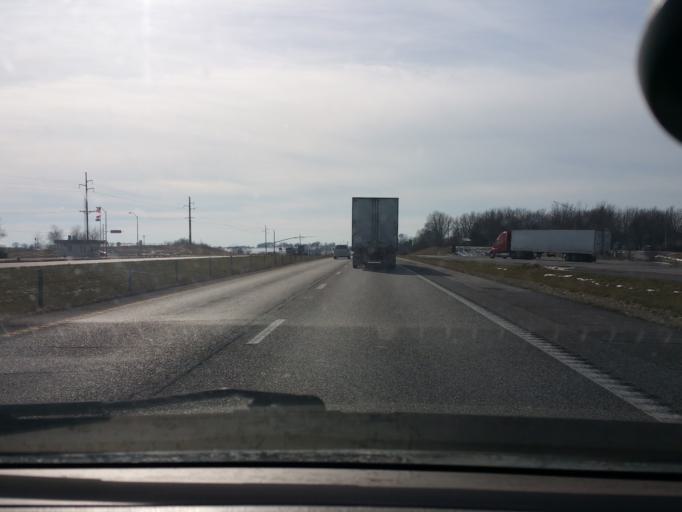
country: US
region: Missouri
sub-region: Clay County
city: Kearney
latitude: 39.3187
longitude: -94.3989
